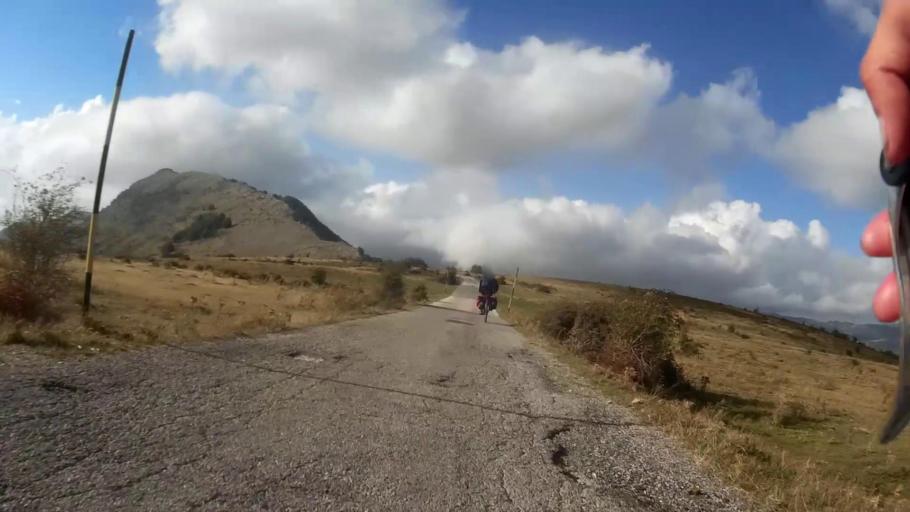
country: IT
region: Basilicate
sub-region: Provincia di Potenza
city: Viggianello
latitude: 39.9534
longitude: 16.1428
